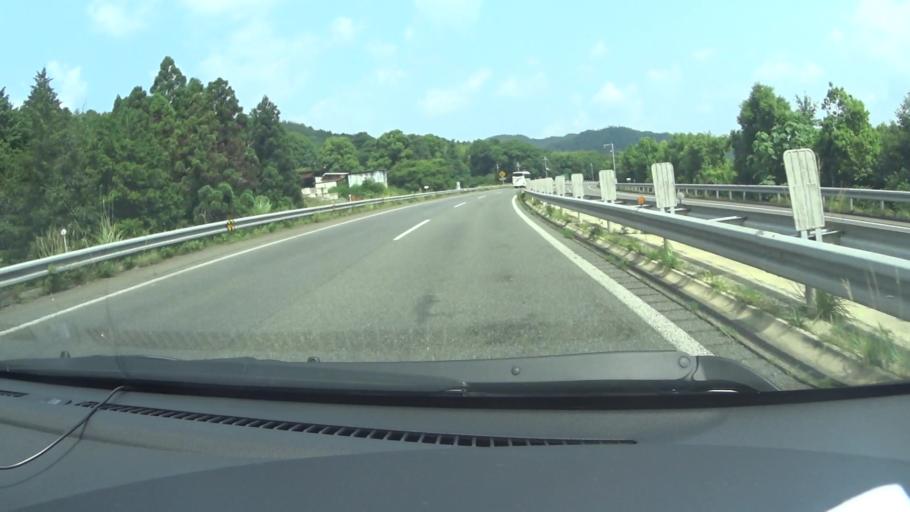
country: JP
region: Kyoto
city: Kameoka
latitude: 35.0425
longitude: 135.5367
